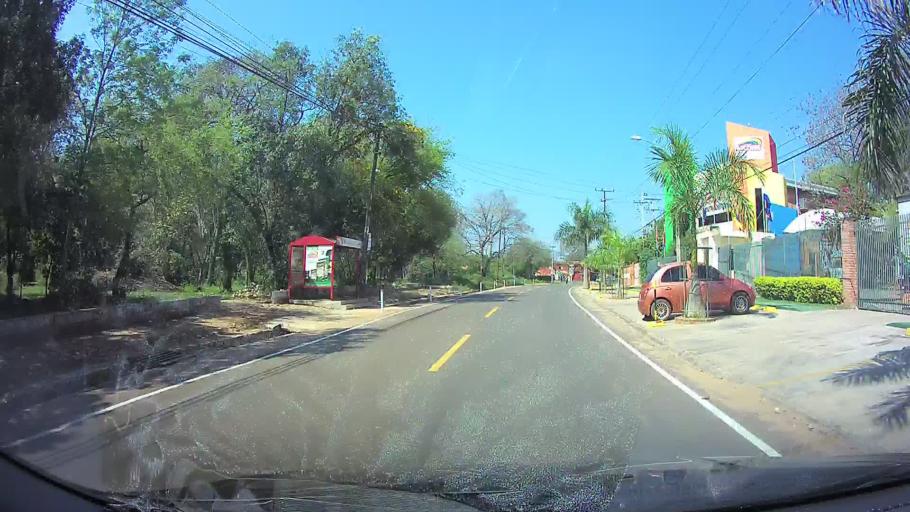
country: PY
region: Central
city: Limpio
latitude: -25.2375
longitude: -57.5068
